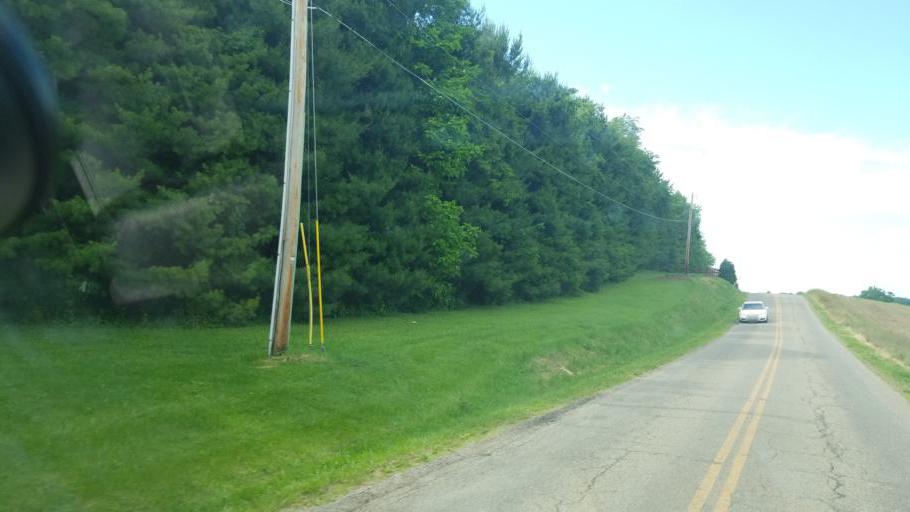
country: US
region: Ohio
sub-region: Knox County
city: Gambier
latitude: 40.2891
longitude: -82.3558
